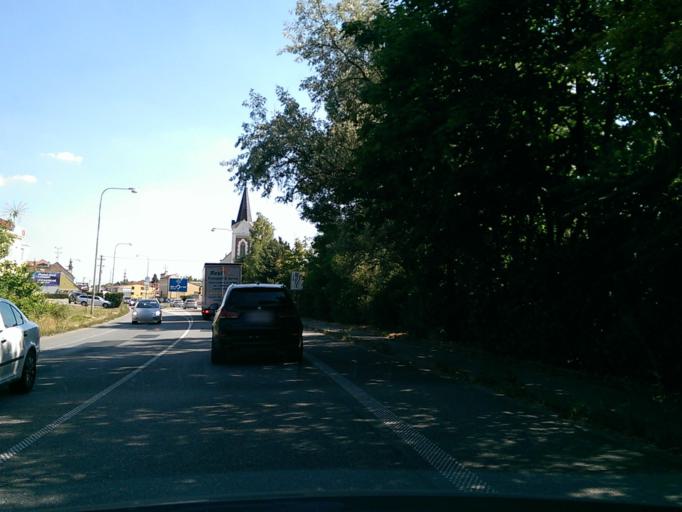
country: CZ
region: South Moravian
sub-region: Okres Breclav
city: Mikulov
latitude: 48.8027
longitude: 16.6274
